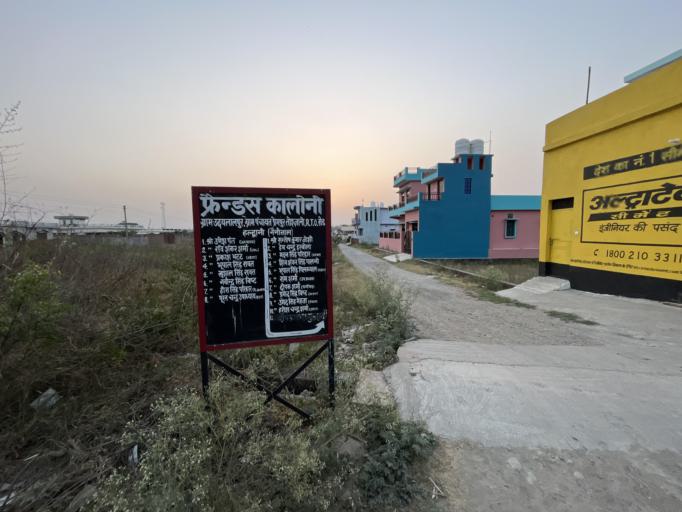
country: IN
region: Uttarakhand
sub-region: Naini Tal
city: Haldwani
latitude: 29.1906
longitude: 79.4697
